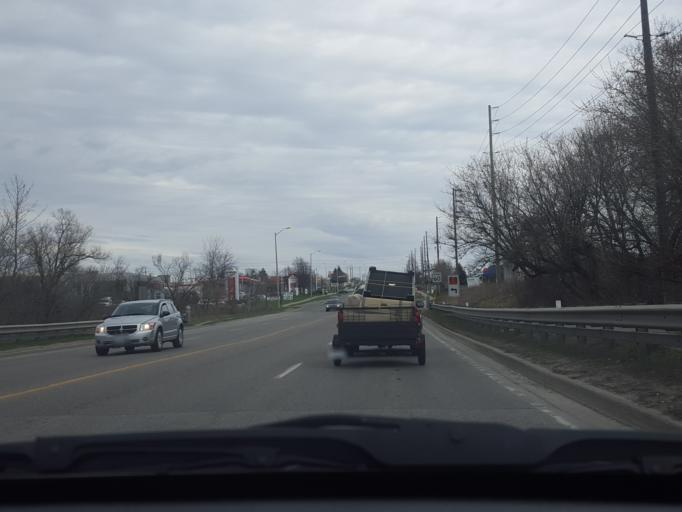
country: CA
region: Ontario
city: Ajax
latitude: 43.8392
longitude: -79.0393
